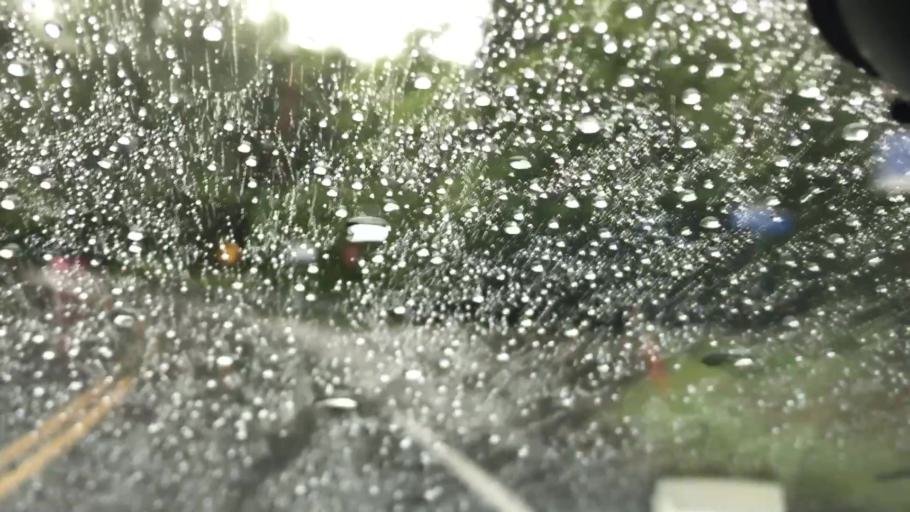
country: US
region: Pennsylvania
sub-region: Allegheny County
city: Allison Park
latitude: 40.5570
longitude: -79.9733
